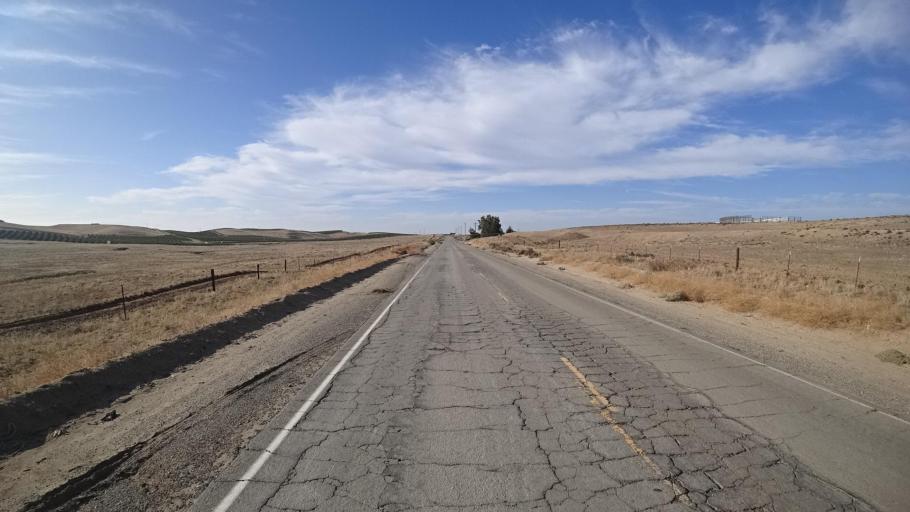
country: US
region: California
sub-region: Kern County
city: McFarland
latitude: 35.6063
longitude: -119.0659
